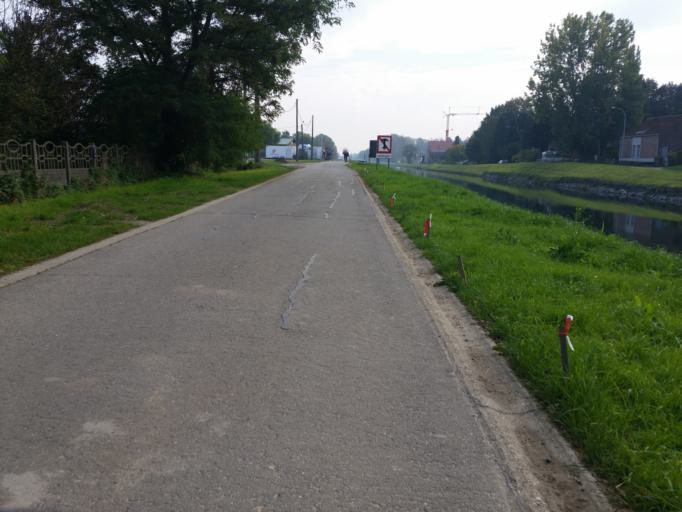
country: BE
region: Flanders
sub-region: Provincie Antwerpen
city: Mechelen
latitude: 51.0061
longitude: 4.4988
